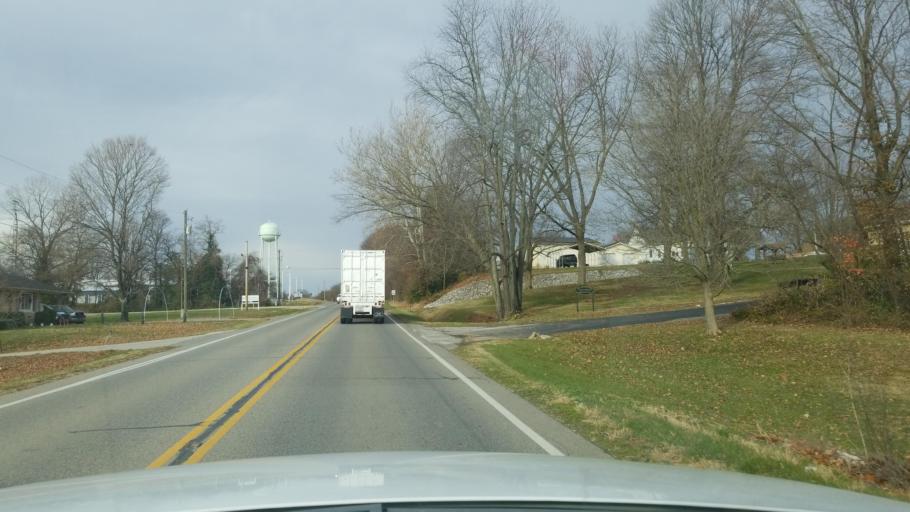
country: US
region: Indiana
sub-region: Posey County
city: Mount Vernon
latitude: 37.9280
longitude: -87.9173
